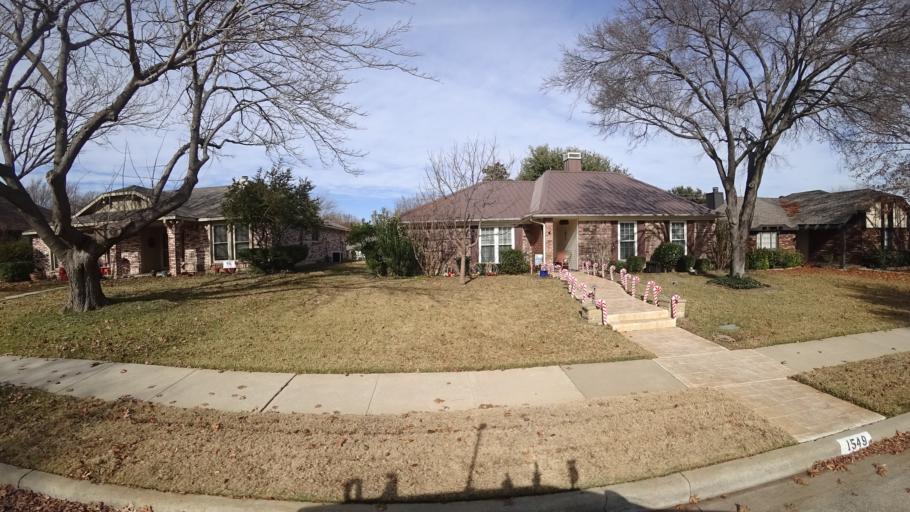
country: US
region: Texas
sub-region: Denton County
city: Highland Village
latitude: 33.0613
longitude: -97.0388
